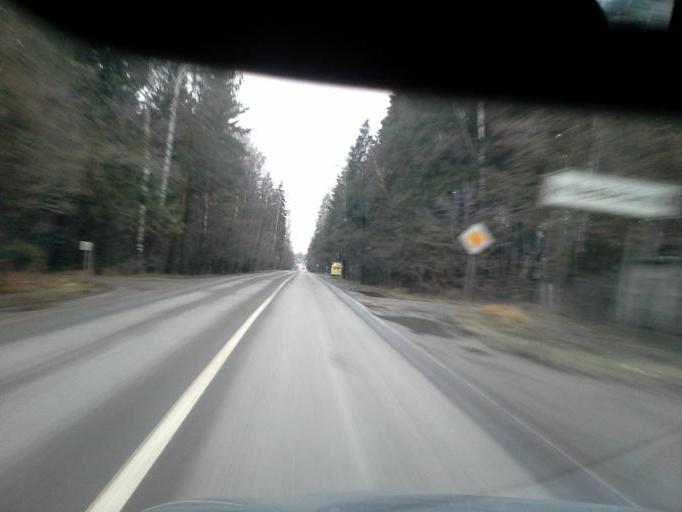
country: RU
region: Moskovskaya
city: Zhavoronki
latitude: 55.6313
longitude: 37.0986
